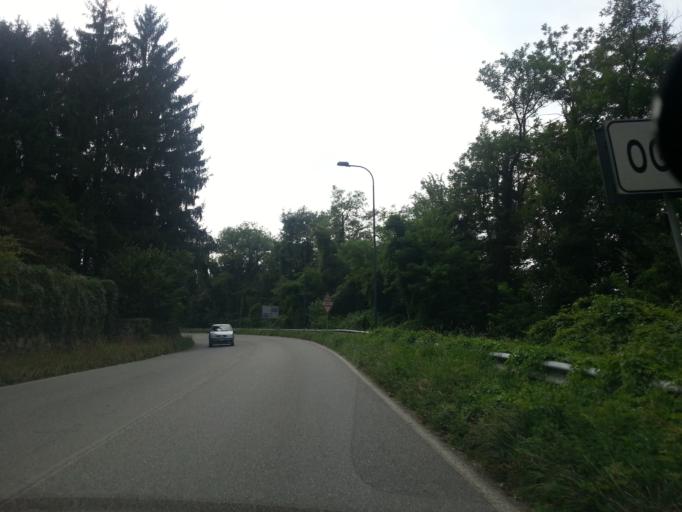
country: IT
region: Lombardy
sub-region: Provincia di Lecco
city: Oggiono
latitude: 45.7949
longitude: 9.3551
